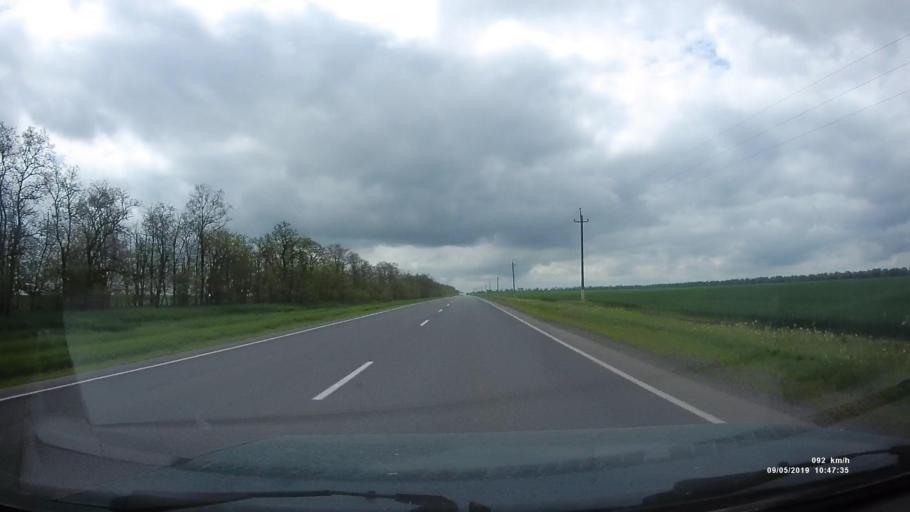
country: RU
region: Rostov
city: Peshkovo
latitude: 46.9687
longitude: 39.3556
